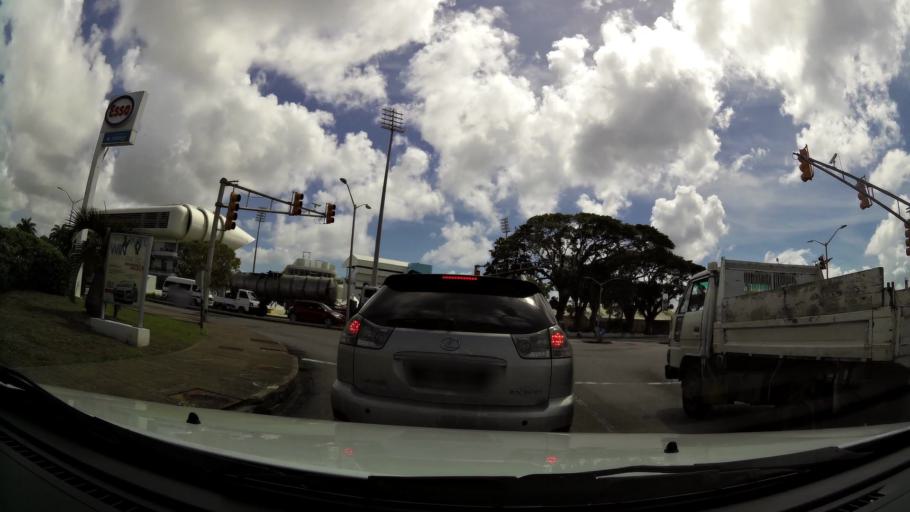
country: BB
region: Saint Michael
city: Bridgetown
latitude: 13.1063
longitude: -59.6240
